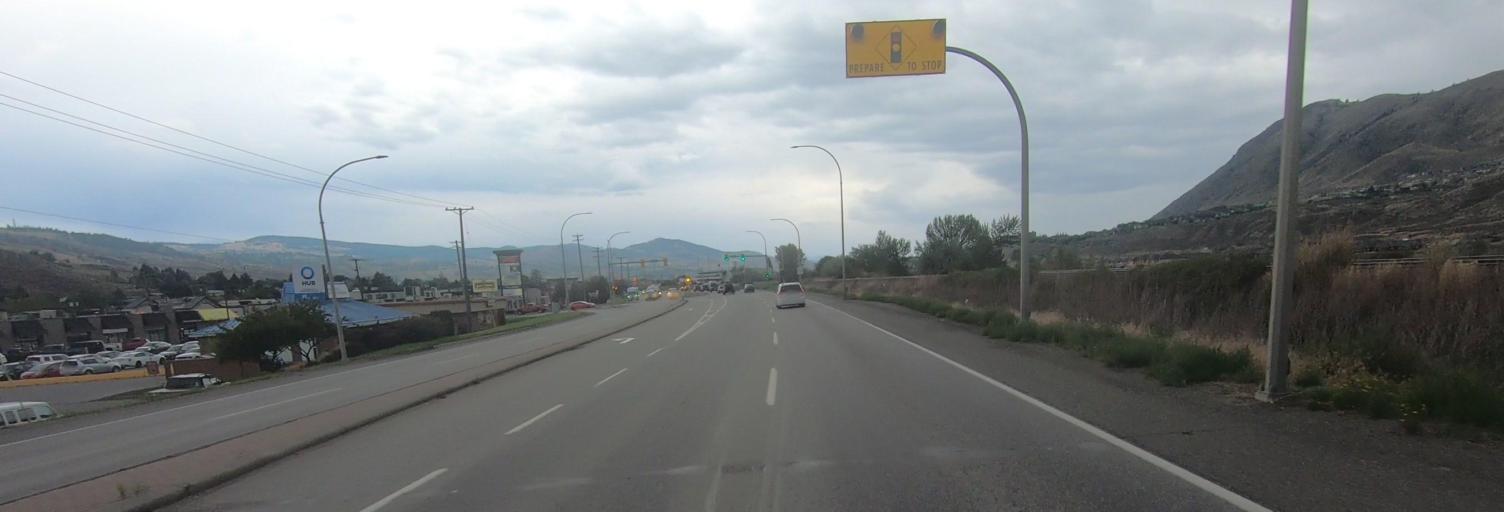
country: CA
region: British Columbia
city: Kamloops
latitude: 50.6806
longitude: -120.2702
